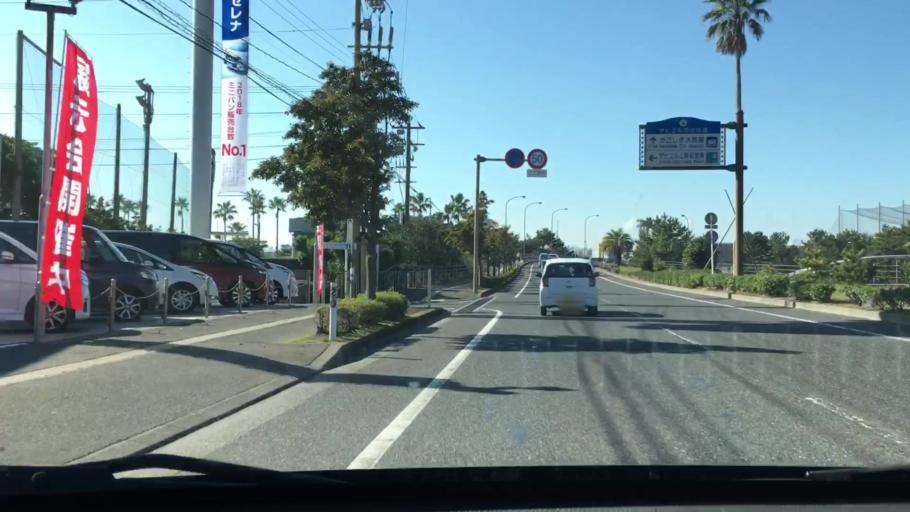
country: JP
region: Kagoshima
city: Kagoshima-shi
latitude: 31.6050
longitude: 130.5715
